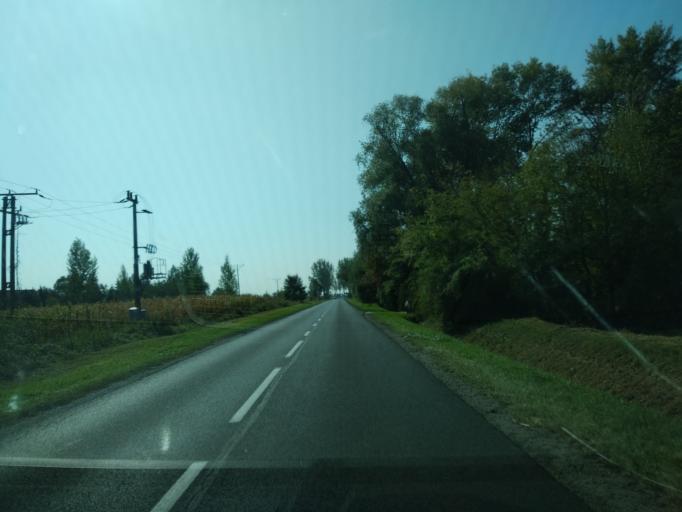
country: PL
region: Lower Silesian Voivodeship
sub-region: Powiat wroclawski
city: Zerniki Wroclawskie
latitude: 51.0268
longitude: 17.0340
